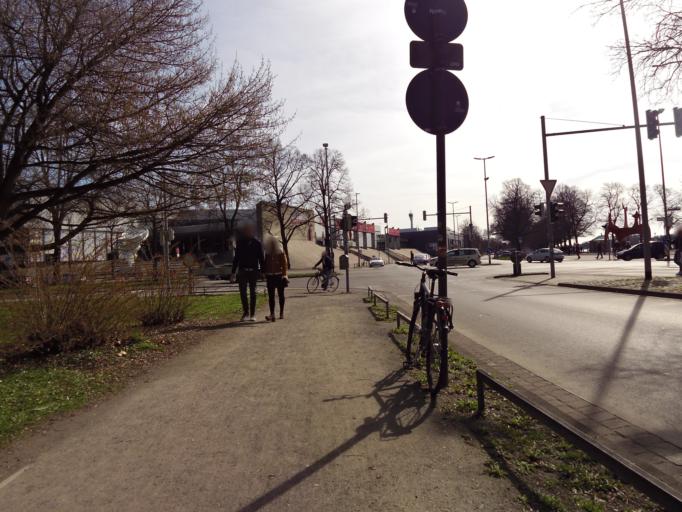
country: DE
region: Lower Saxony
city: Hannover
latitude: 52.3637
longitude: 9.7384
